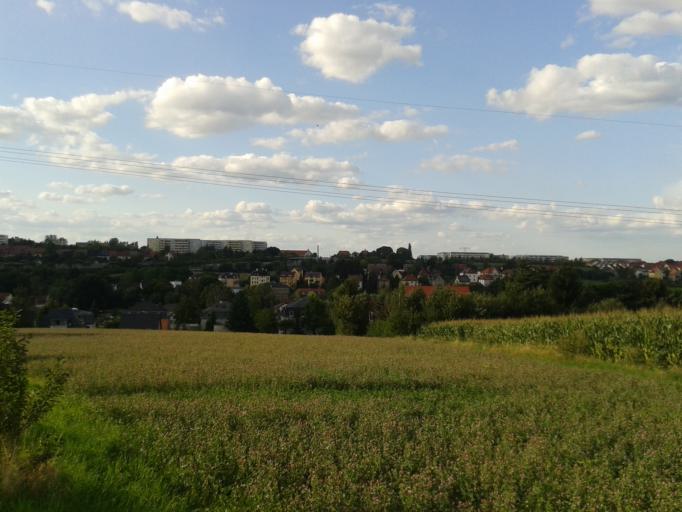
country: DE
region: Saxony
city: Bannewitz
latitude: 51.0105
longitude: 13.7299
